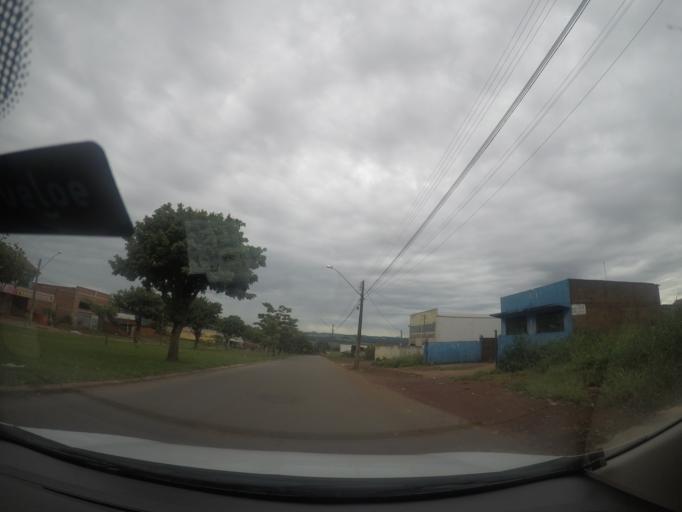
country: BR
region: Goias
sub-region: Goiania
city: Goiania
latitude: -16.6069
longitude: -49.3049
